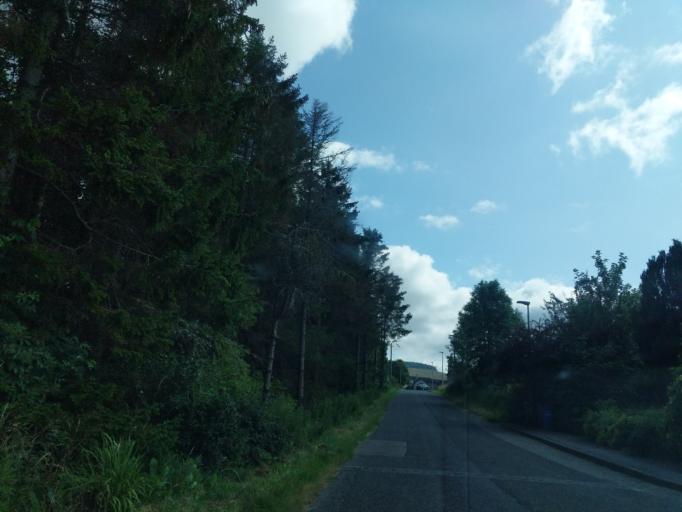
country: GB
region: Scotland
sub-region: Moray
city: Rothes
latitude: 57.4888
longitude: -3.1827
